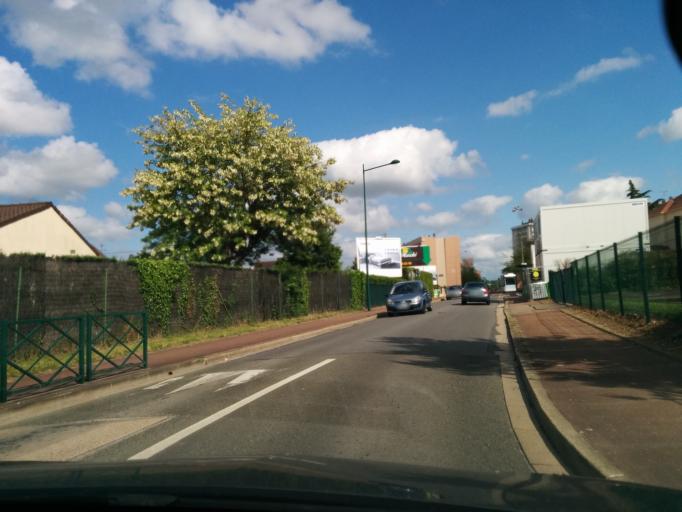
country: FR
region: Ile-de-France
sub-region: Departement des Yvelines
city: Mantes-la-Ville
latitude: 48.9790
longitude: 1.6986
